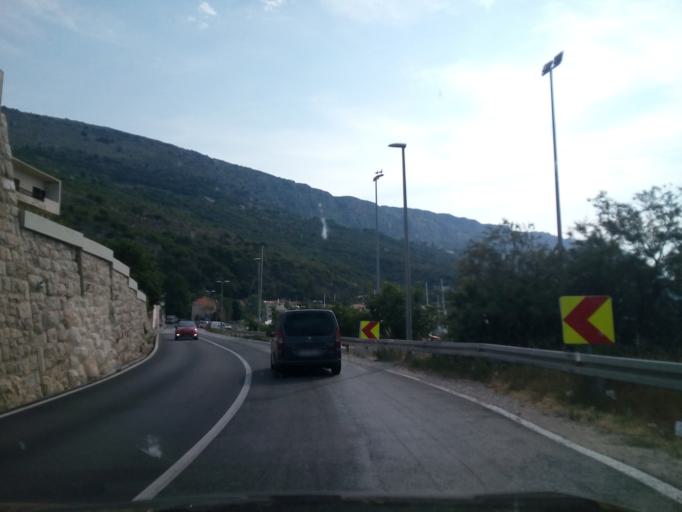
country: HR
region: Splitsko-Dalmatinska
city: Jesenice
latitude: 43.4599
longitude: 16.5958
